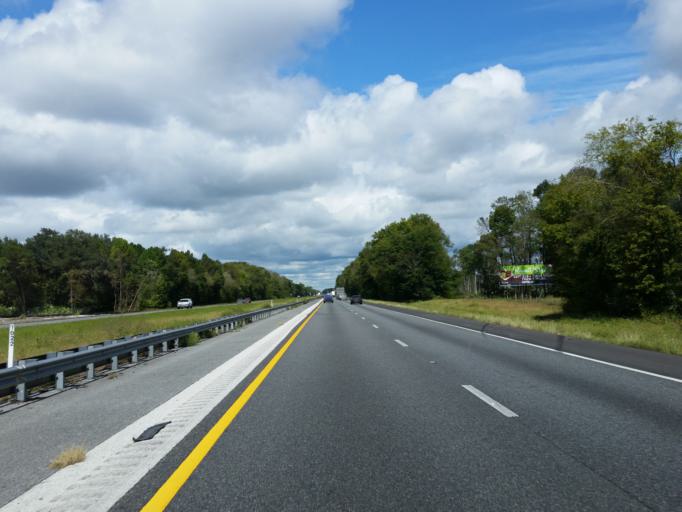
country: US
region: Florida
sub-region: Sumter County
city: Wildwood
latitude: 28.8274
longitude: -82.0896
